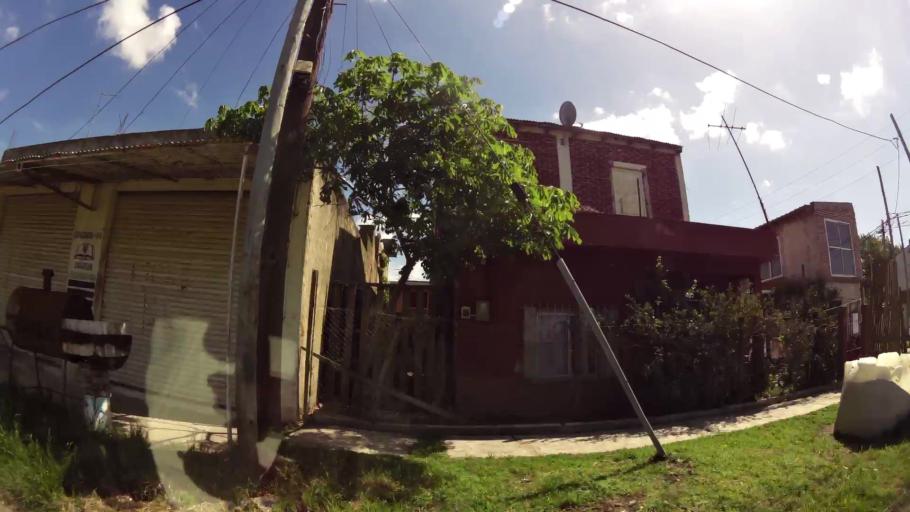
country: AR
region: Buenos Aires
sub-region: Partido de Quilmes
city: Quilmes
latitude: -34.8170
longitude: -58.2582
